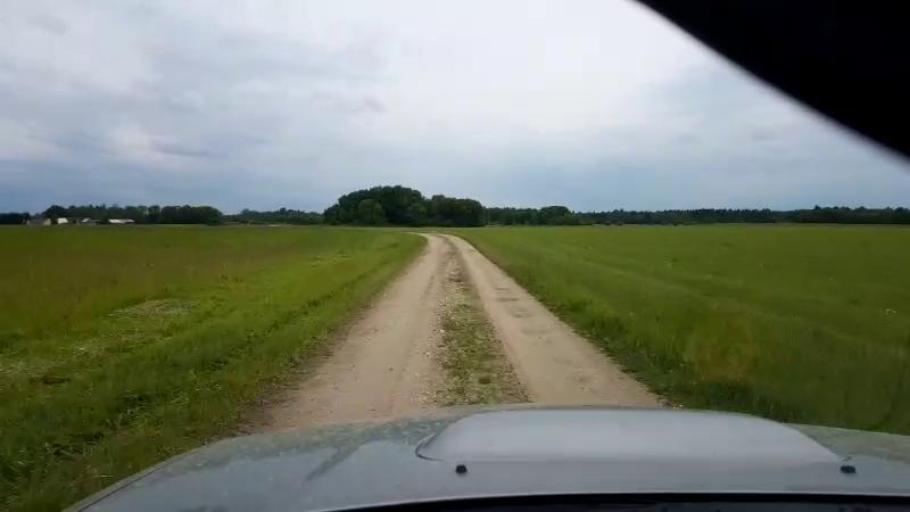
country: EE
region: Paernumaa
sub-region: Tootsi vald
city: Tootsi
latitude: 58.5902
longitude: 24.6588
